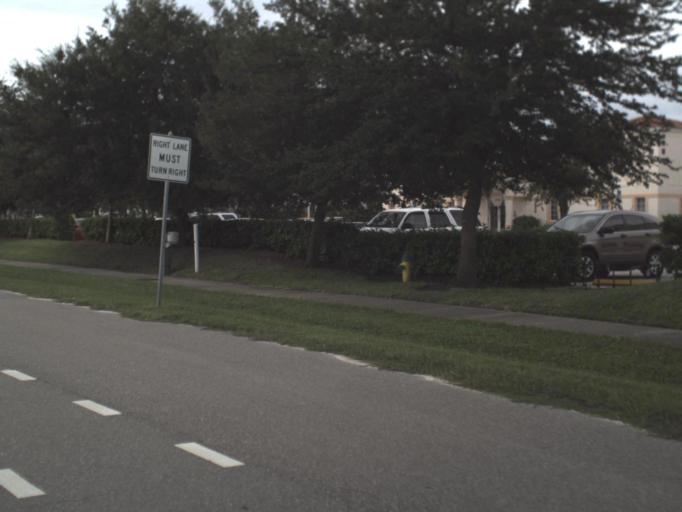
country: US
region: Florida
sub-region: Sarasota County
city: Venice Gardens
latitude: 27.0998
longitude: -82.4014
